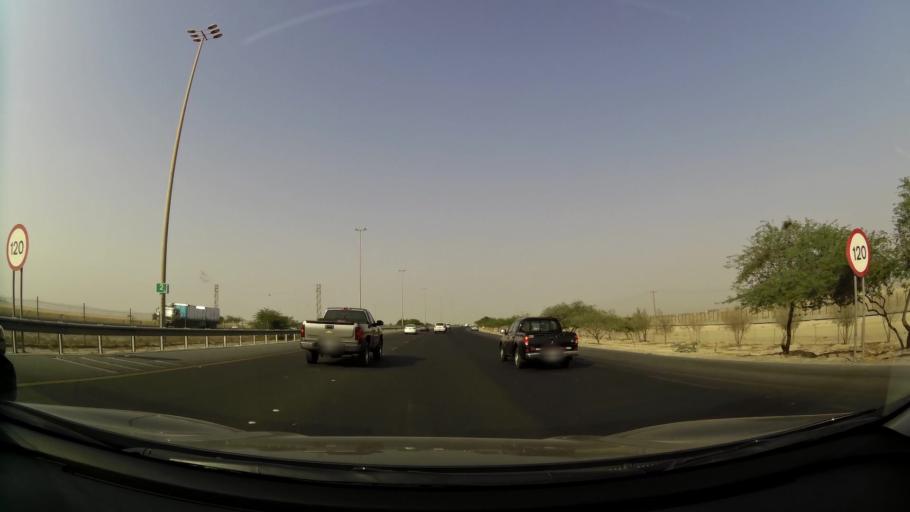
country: KW
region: Mubarak al Kabir
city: Mubarak al Kabir
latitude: 29.1728
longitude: 48.0480
